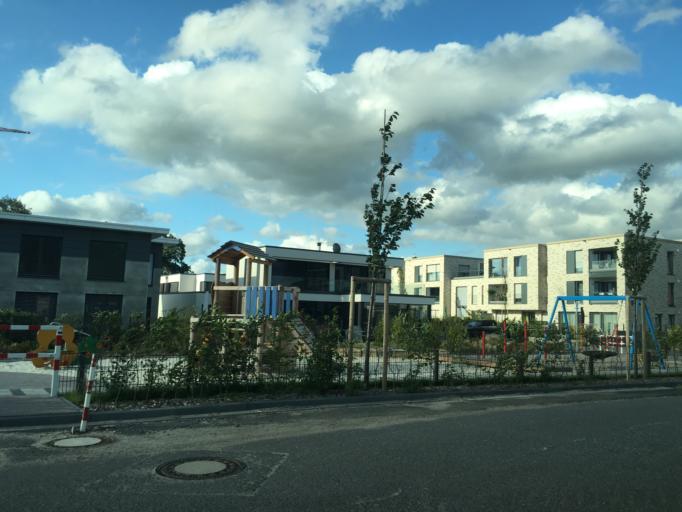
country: DE
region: North Rhine-Westphalia
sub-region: Regierungsbezirk Munster
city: Muenster
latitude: 51.9771
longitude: 7.6088
